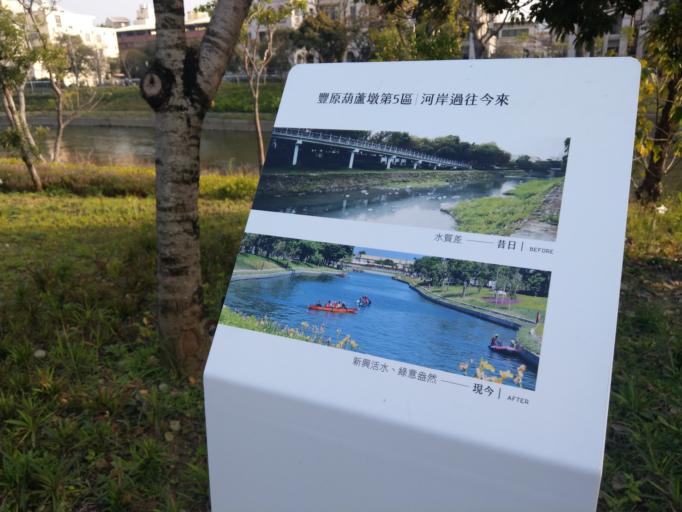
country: TW
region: Taiwan
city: Fengyuan
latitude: 24.2561
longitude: 120.7084
